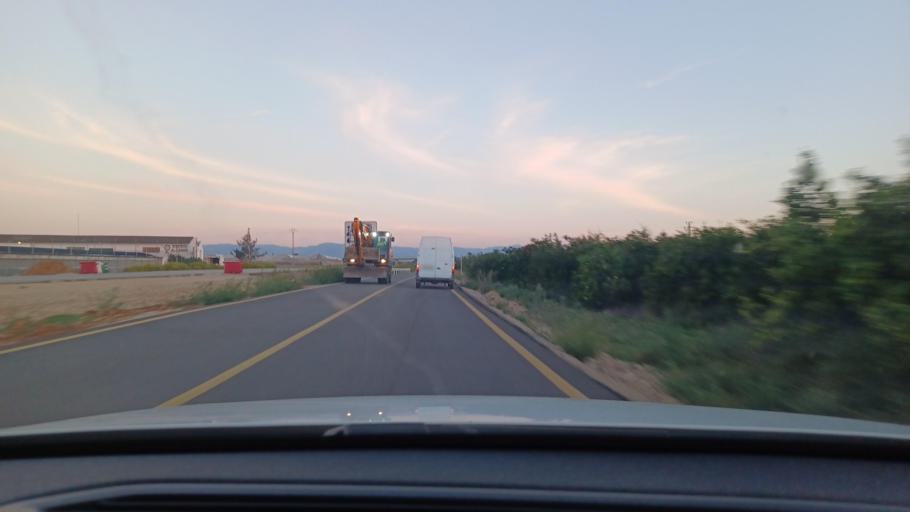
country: ES
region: Catalonia
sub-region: Provincia de Tarragona
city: Alcanar
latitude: 40.5407
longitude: 0.4392
